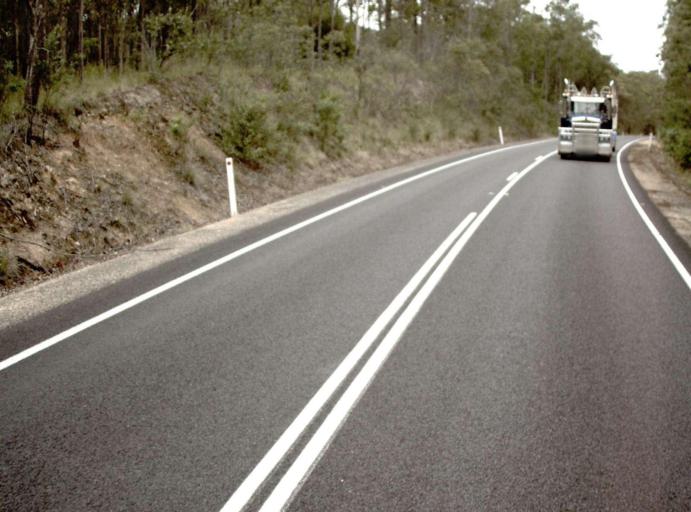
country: AU
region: New South Wales
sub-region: Bombala
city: Bombala
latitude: -37.3207
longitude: 149.2068
